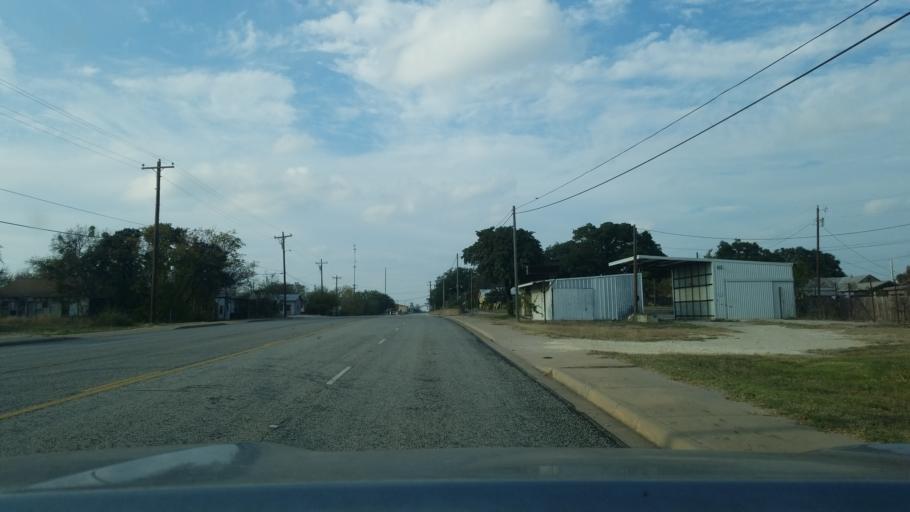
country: US
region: Texas
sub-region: Lampasas County
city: Lampasas
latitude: 31.2115
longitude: -98.3908
